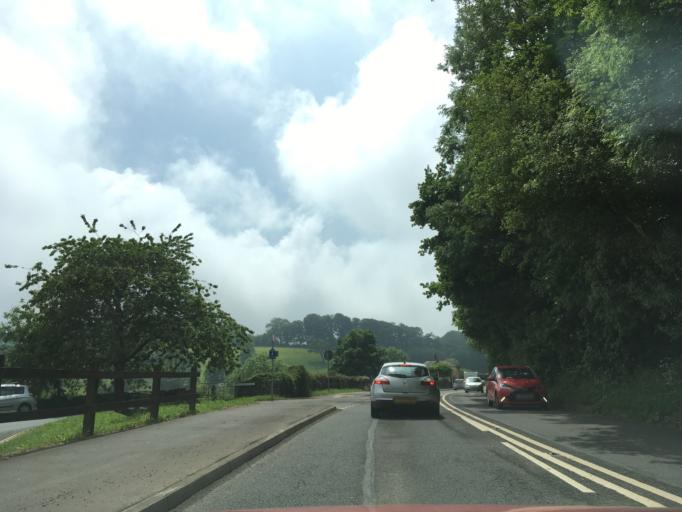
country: GB
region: England
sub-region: Devon
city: Totnes
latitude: 50.4262
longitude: -3.6906
